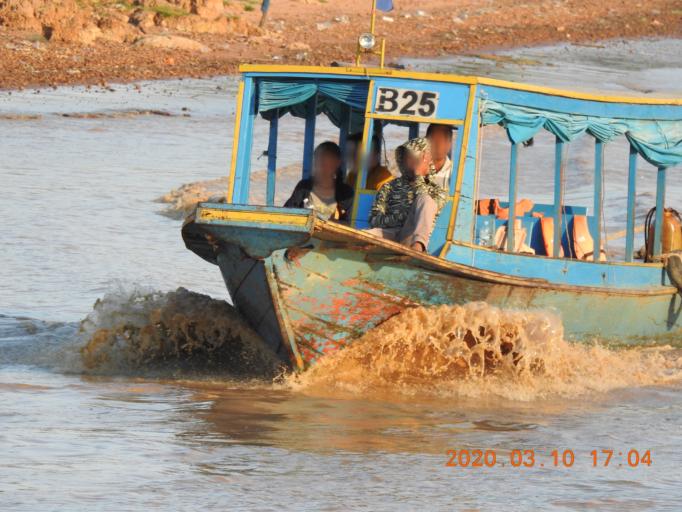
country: KH
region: Siem Reap
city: Siem Reap
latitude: 13.2407
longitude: 103.8248
